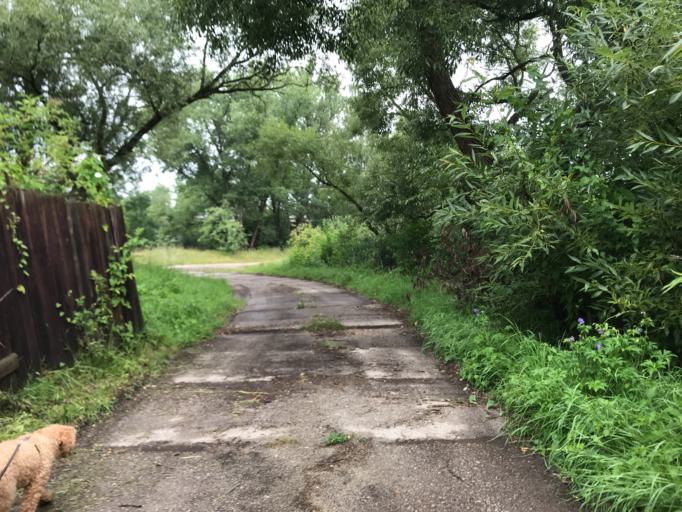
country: CZ
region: Jihocesky
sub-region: Okres Jindrichuv Hradec
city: Trebon
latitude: 49.0094
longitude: 14.7665
